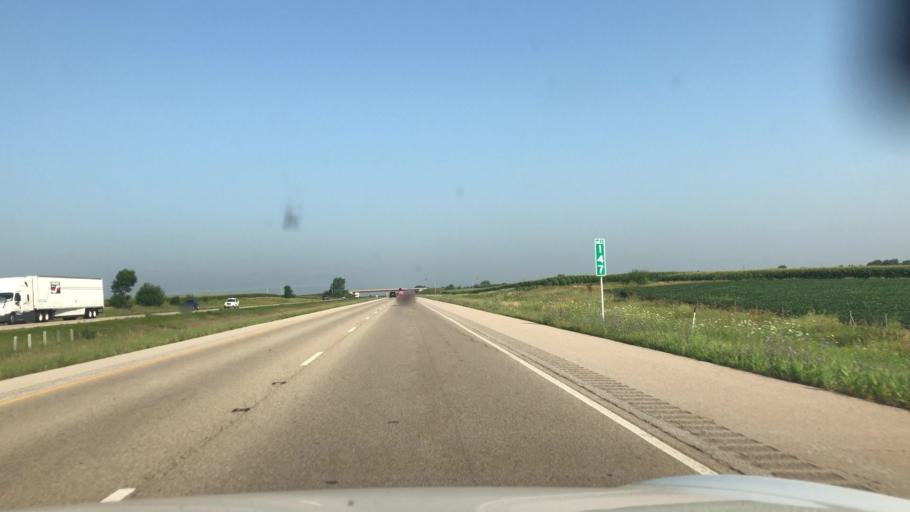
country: US
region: Illinois
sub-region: McLean County
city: Le Roy
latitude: 40.3561
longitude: -88.8017
